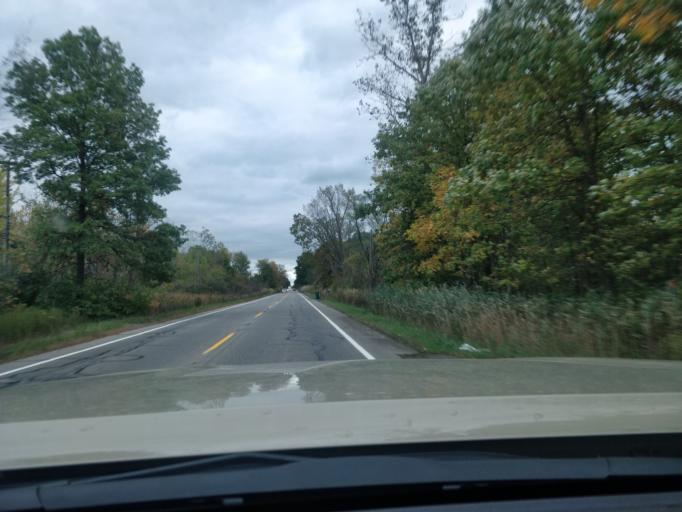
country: US
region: Michigan
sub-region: Wayne County
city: Romulus
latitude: 42.1806
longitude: -83.3526
